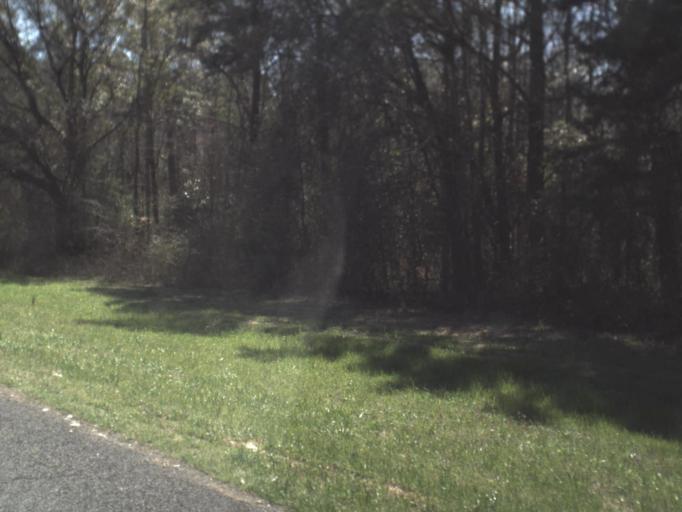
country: US
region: Florida
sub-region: Jackson County
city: Graceville
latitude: 30.9615
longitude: -85.4046
